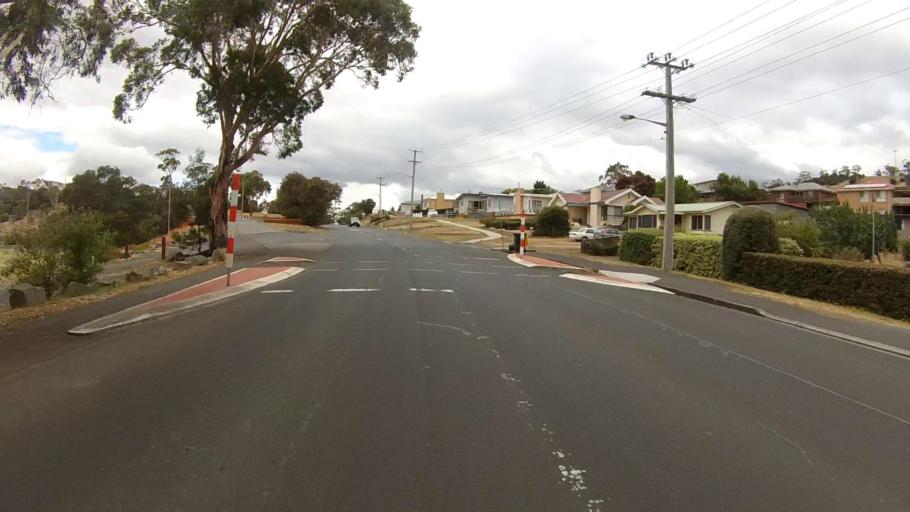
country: AU
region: Tasmania
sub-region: Glenorchy
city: Austins Ferry
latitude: -42.7727
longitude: 147.2482
